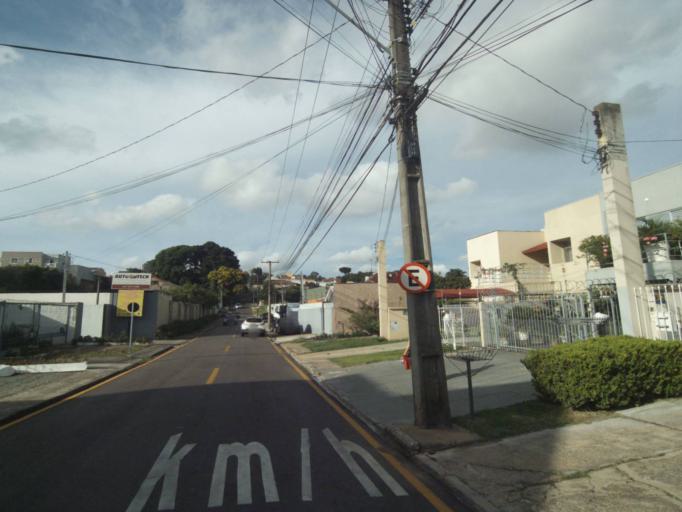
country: BR
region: Parana
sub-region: Curitiba
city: Curitiba
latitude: -25.4458
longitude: -49.3088
